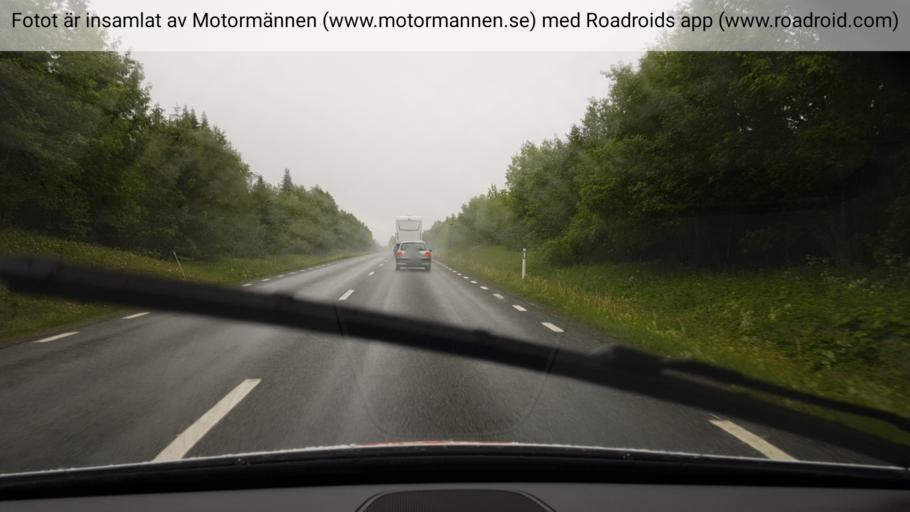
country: SE
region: Jaemtland
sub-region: OEstersunds Kommun
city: Lit
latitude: 63.4564
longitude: 15.1731
